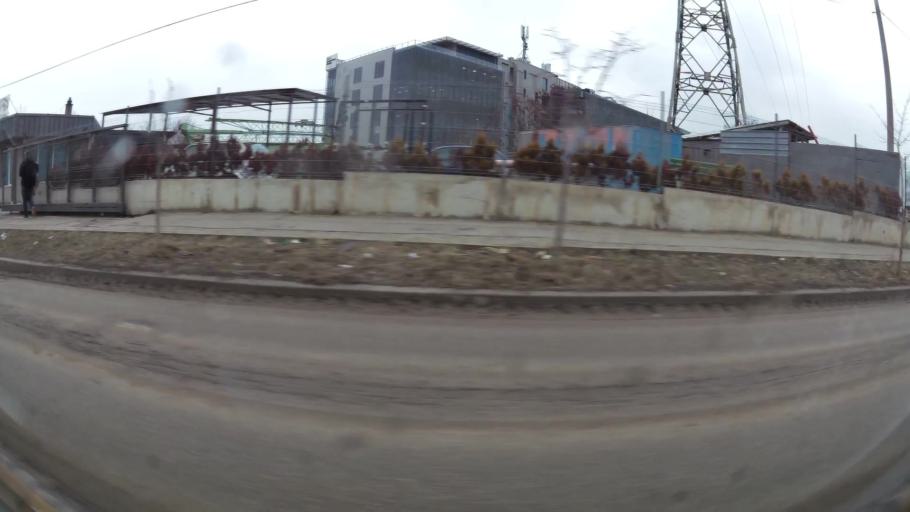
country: BG
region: Sofia-Capital
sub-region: Stolichna Obshtina
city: Sofia
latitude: 42.6221
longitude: 23.3772
